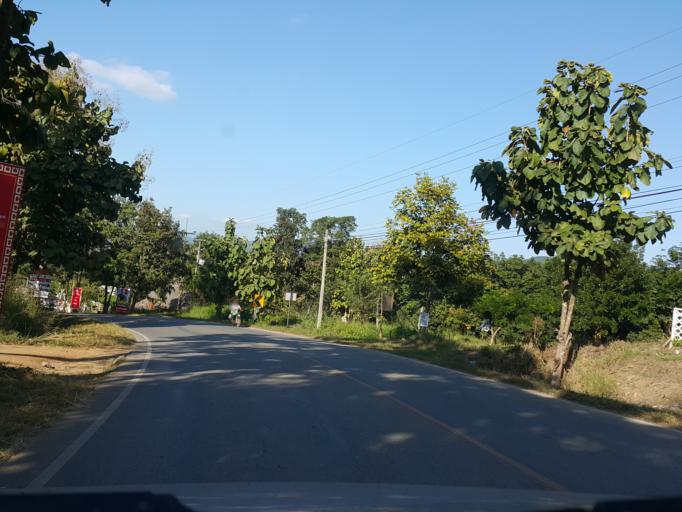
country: TH
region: Mae Hong Son
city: Mae Hi
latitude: 19.3392
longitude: 98.4334
